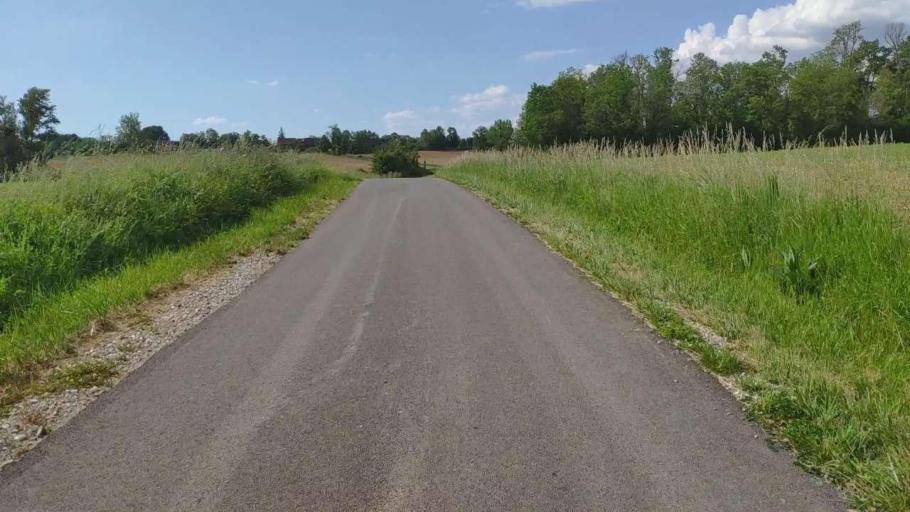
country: FR
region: Franche-Comte
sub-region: Departement du Jura
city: Bletterans
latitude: 46.8154
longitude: 5.3702
